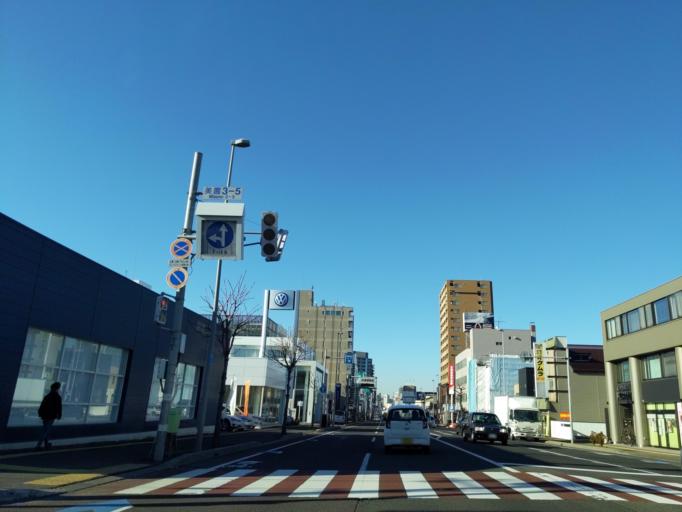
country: JP
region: Hokkaido
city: Sapporo
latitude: 43.0409
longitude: 141.3883
